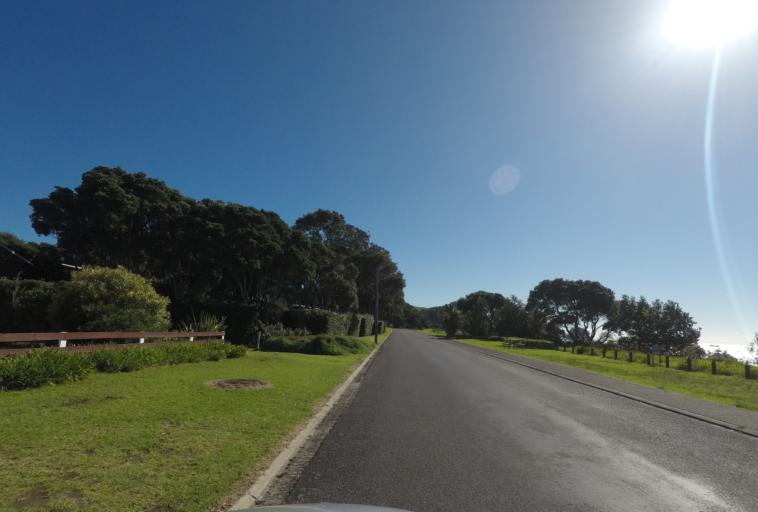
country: NZ
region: Waikato
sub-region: Thames-Coromandel District
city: Whangamata
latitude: -37.2818
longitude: 175.9018
